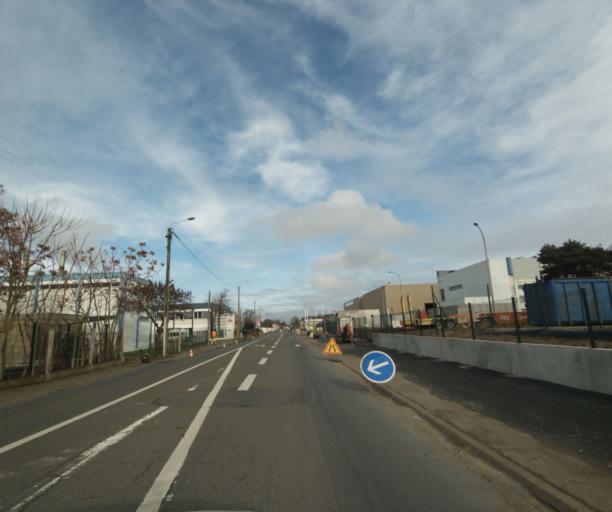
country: FR
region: Pays de la Loire
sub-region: Departement de la Sarthe
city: Allonnes
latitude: 47.9754
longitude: 0.1752
